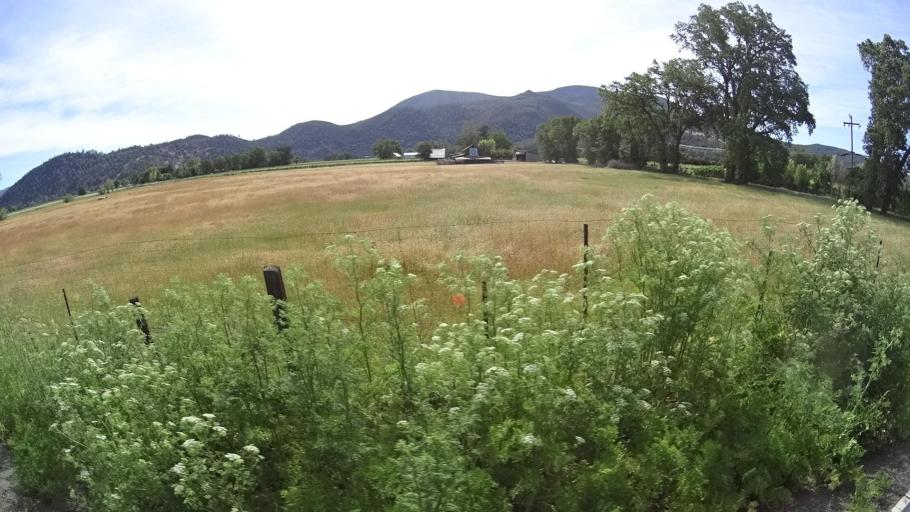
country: US
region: California
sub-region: Lake County
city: Kelseyville
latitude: 38.9897
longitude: -122.8291
